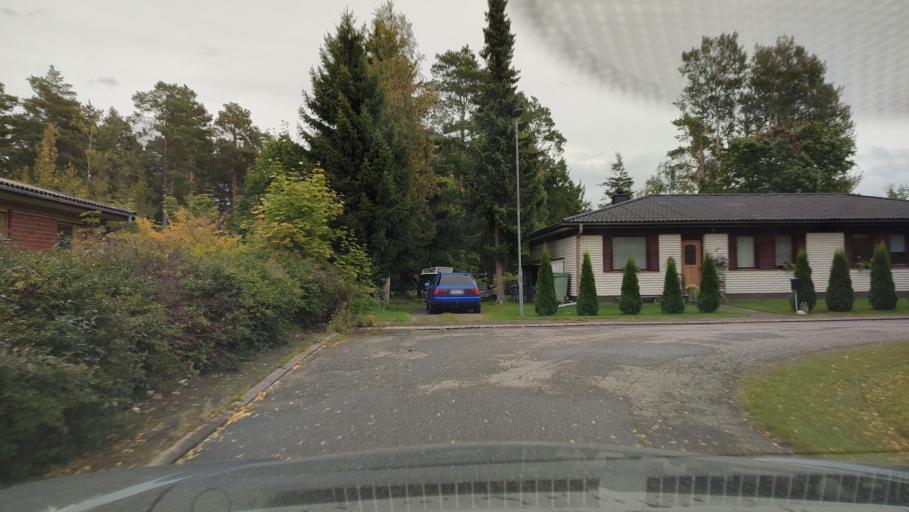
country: FI
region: Ostrobothnia
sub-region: Sydosterbotten
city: Kristinestad
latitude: 62.2828
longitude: 21.3594
